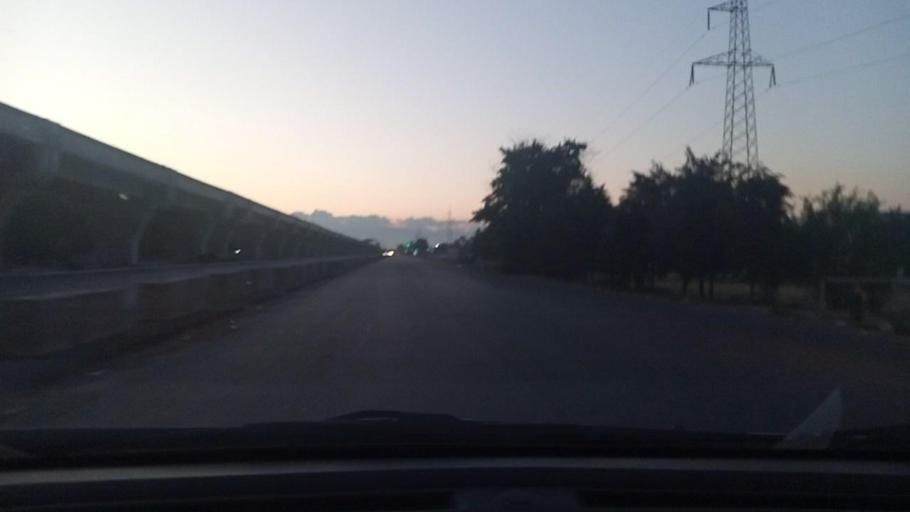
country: UZ
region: Toshkent Shahri
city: Bektemir
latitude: 41.2443
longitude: 69.2897
